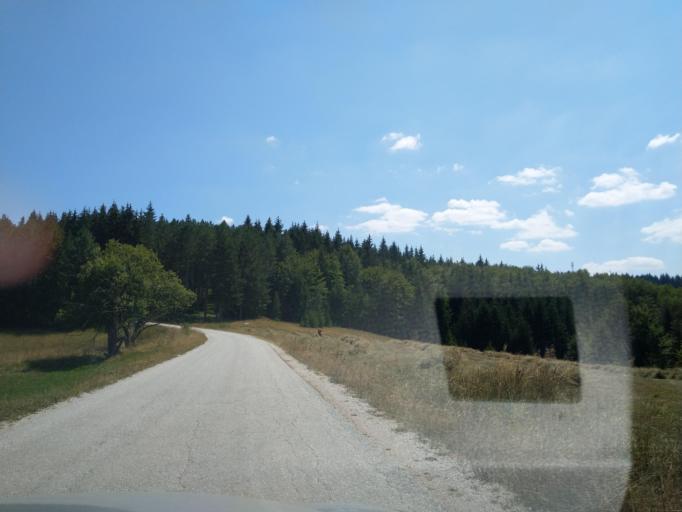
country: RS
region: Central Serbia
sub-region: Zlatiborski Okrug
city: Nova Varos
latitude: 43.4691
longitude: 19.9674
